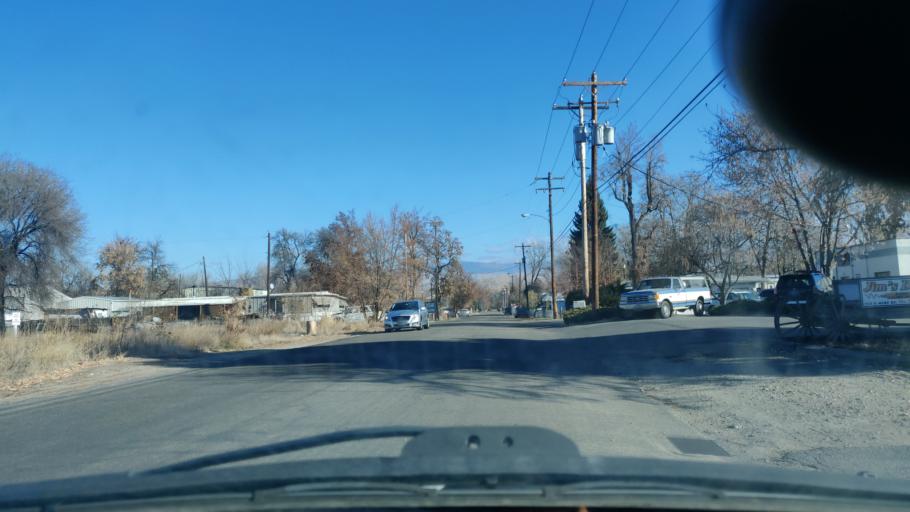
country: US
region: Idaho
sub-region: Ada County
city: Garden City
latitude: 43.6306
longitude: -116.2489
